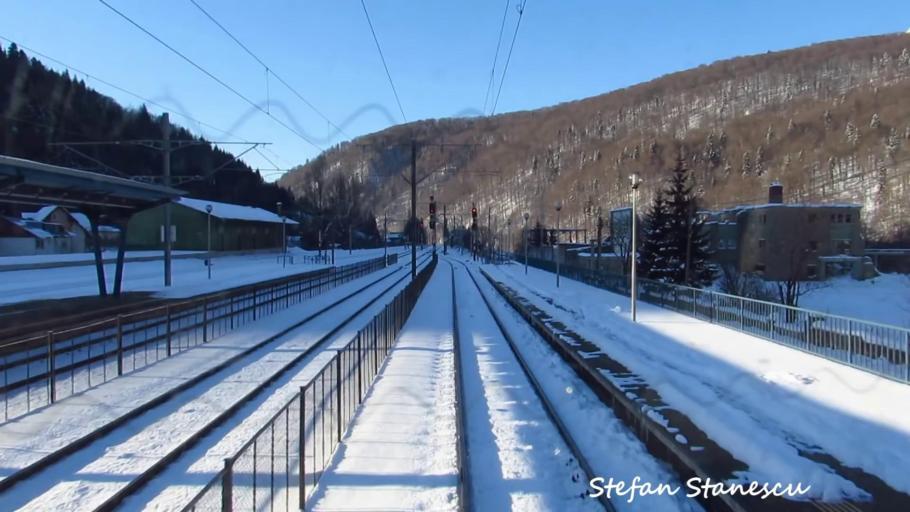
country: RO
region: Prahova
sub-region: Oras Azuga
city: Azuga
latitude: 45.4420
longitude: 25.5510
